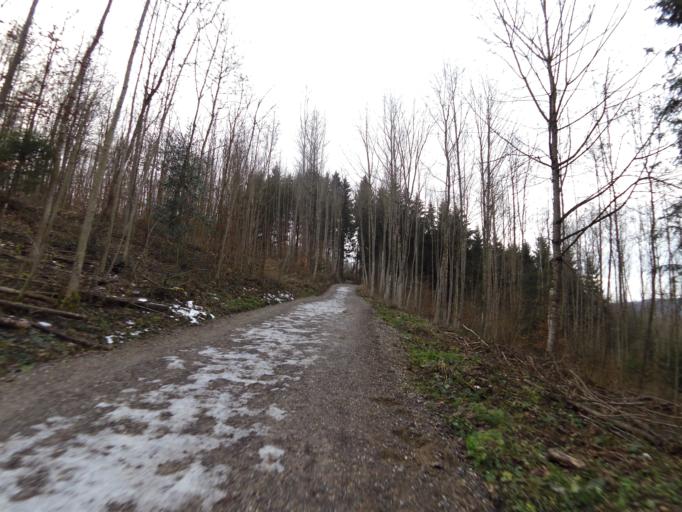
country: CH
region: Zurich
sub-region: Bezirk Dietikon
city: Schlieren / Boden
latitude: 47.3865
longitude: 8.4621
